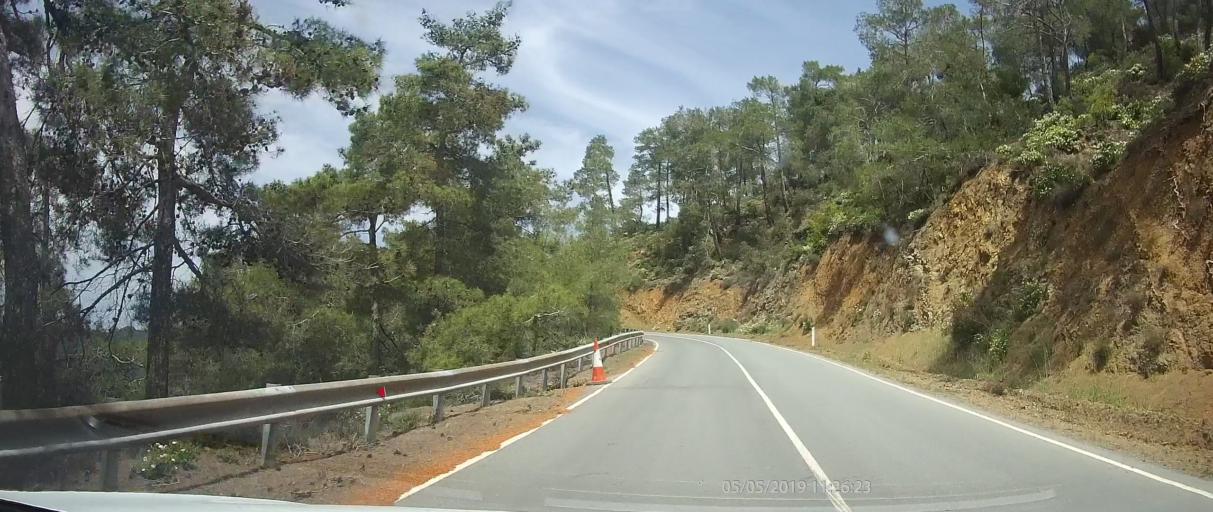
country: CY
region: Limassol
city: Pachna
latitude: 34.9281
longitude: 32.6469
